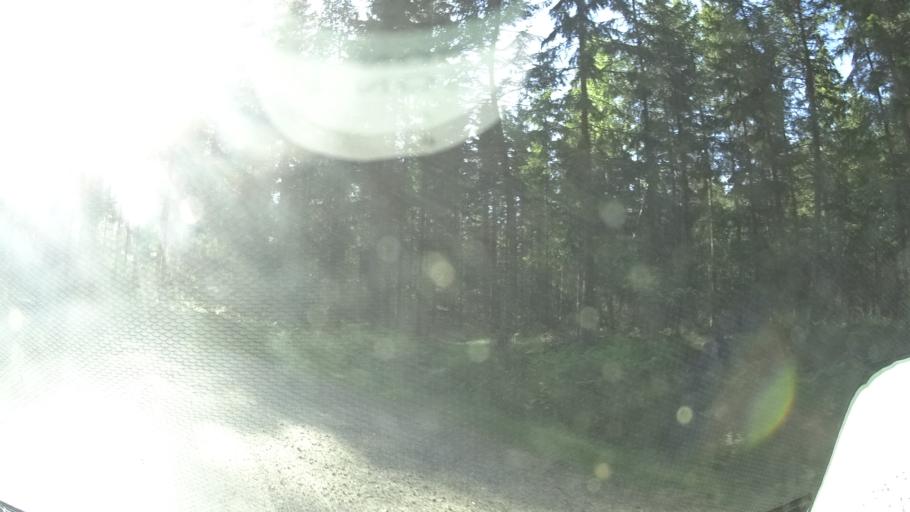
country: SE
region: OEstergoetland
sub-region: Finspangs Kommun
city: Finspang
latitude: 58.6114
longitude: 15.6792
